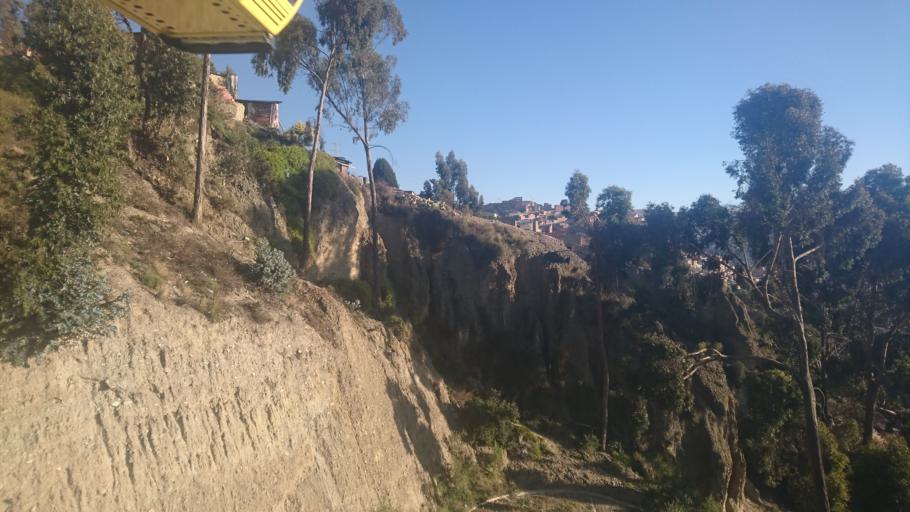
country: BO
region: La Paz
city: La Paz
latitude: -16.5161
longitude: -68.1457
